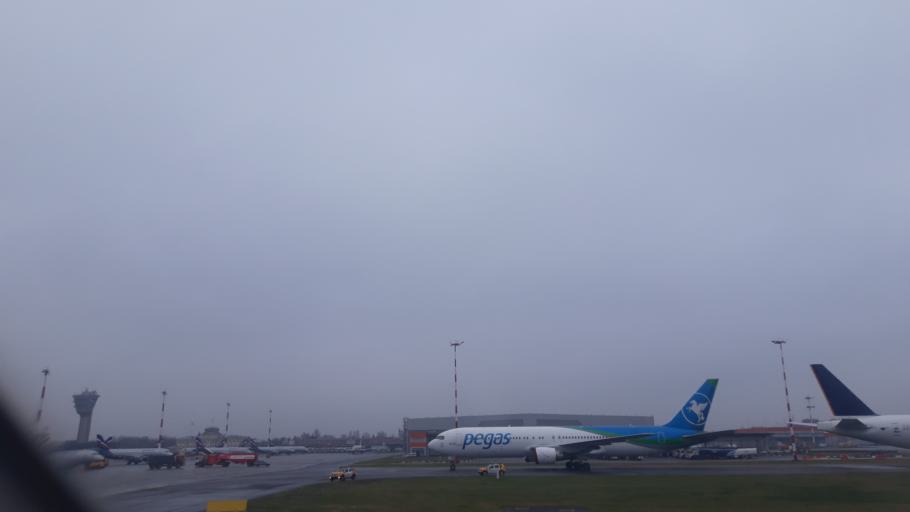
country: RU
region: Moskovskaya
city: Lobnya
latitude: 55.9773
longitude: 37.4249
